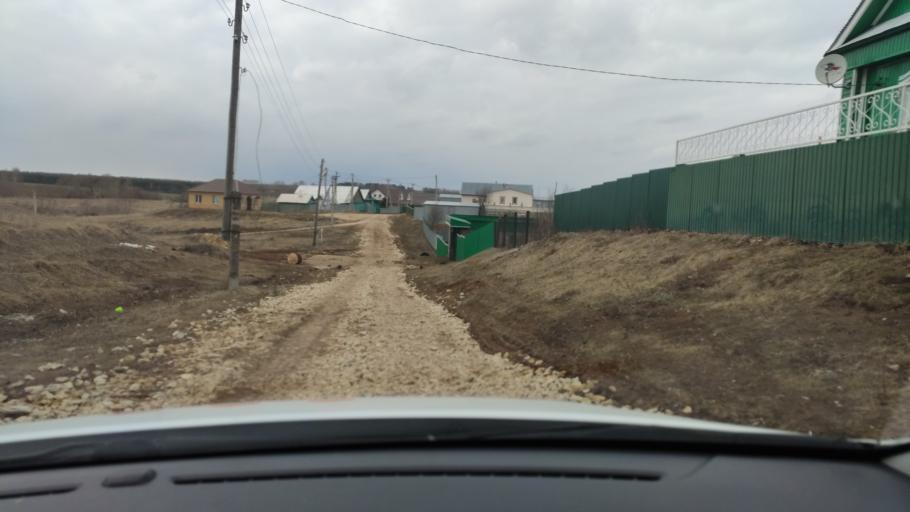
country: RU
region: Tatarstan
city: Vysokaya Gora
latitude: 56.2096
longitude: 49.3146
